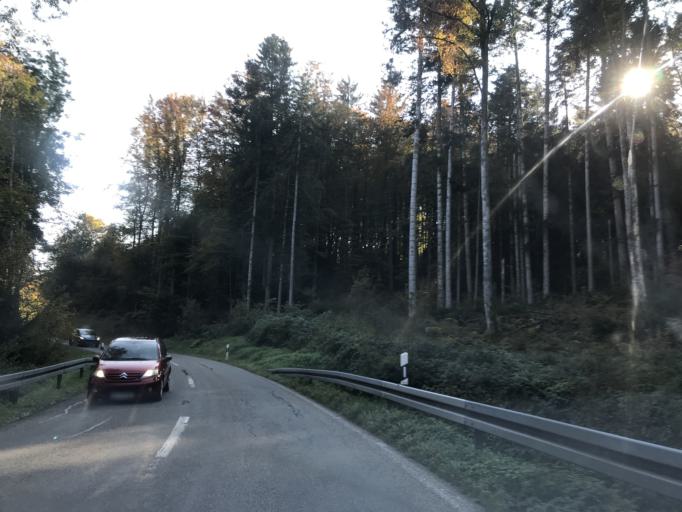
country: DE
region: Baden-Wuerttemberg
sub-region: Freiburg Region
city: Gorwihl
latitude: 47.6281
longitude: 8.0503
